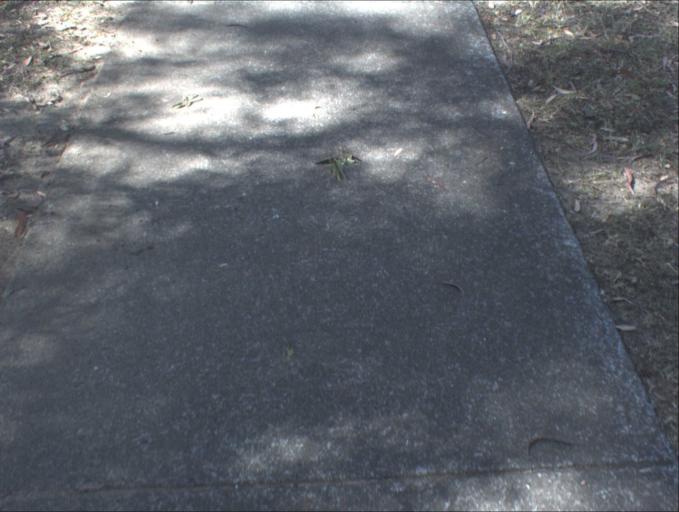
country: AU
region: Queensland
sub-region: Logan
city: Slacks Creek
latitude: -27.6443
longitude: 153.1866
